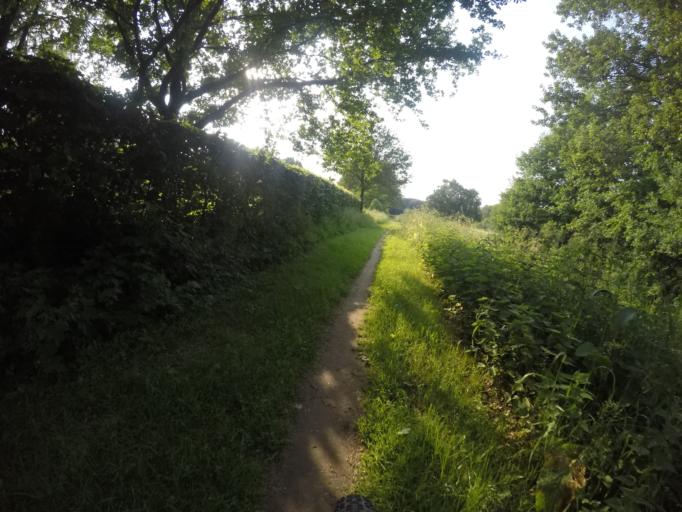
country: DE
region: North Rhine-Westphalia
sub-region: Regierungsbezirk Munster
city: Isselburg
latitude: 51.8366
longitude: 6.4382
